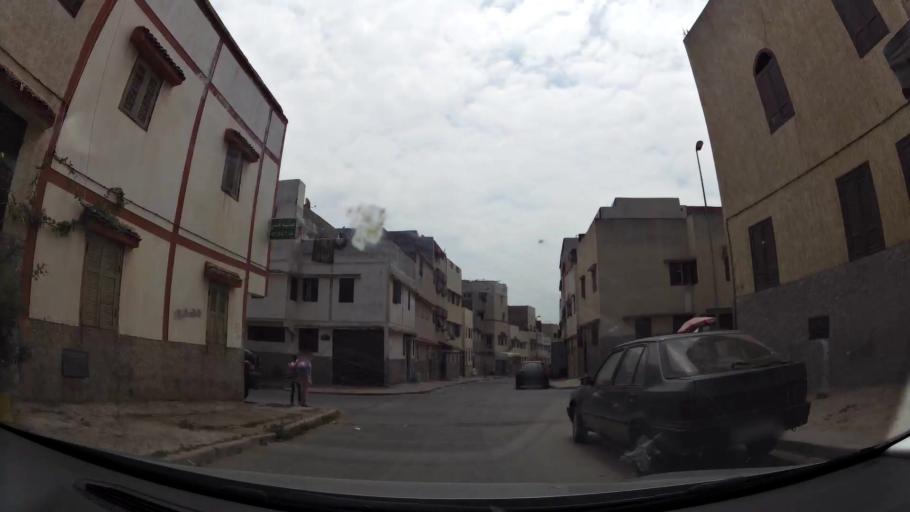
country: MA
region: Rabat-Sale-Zemmour-Zaer
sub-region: Rabat
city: Rabat
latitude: 33.9867
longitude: -6.8874
